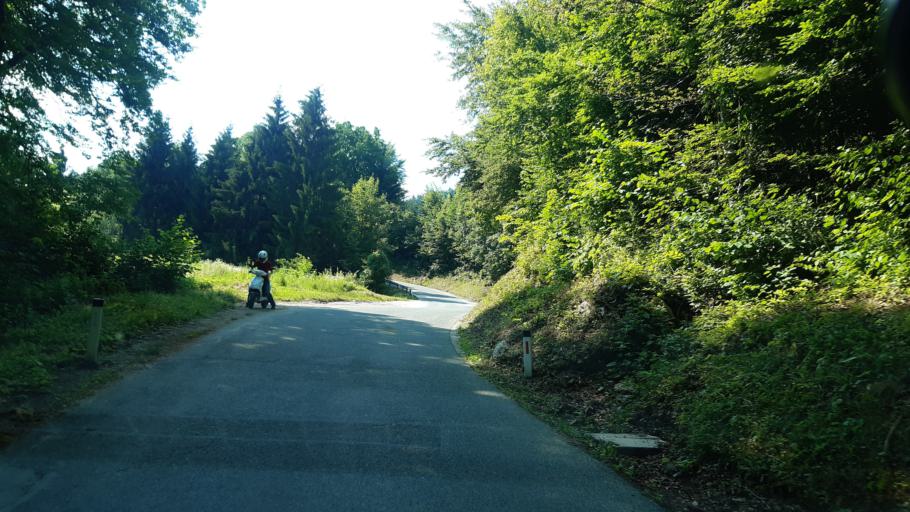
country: SI
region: Trzic
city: Bistrica pri Trzicu
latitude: 46.3604
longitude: 14.2451
